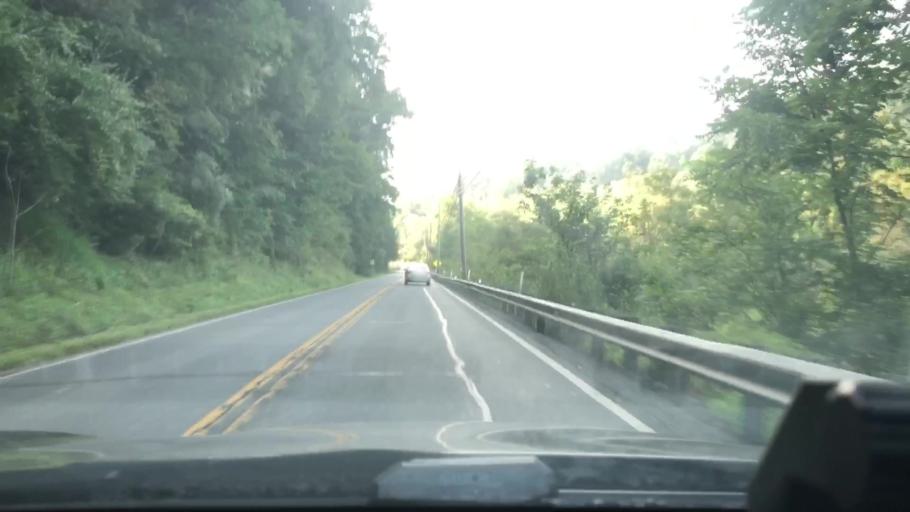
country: US
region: Pennsylvania
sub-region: Berks County
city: Kutztown
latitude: 40.5509
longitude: -75.8014
